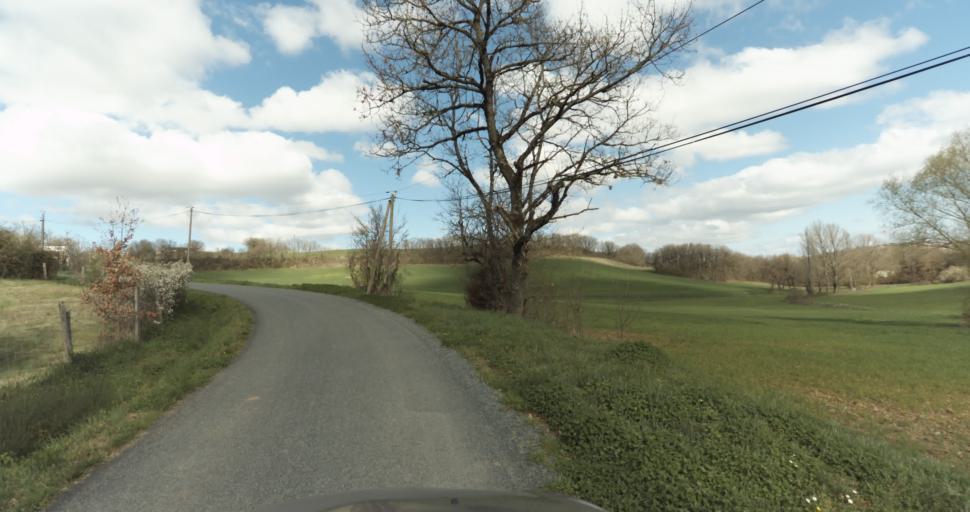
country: FR
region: Midi-Pyrenees
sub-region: Departement du Tarn
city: Puygouzon
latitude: 43.8766
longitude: 2.1631
